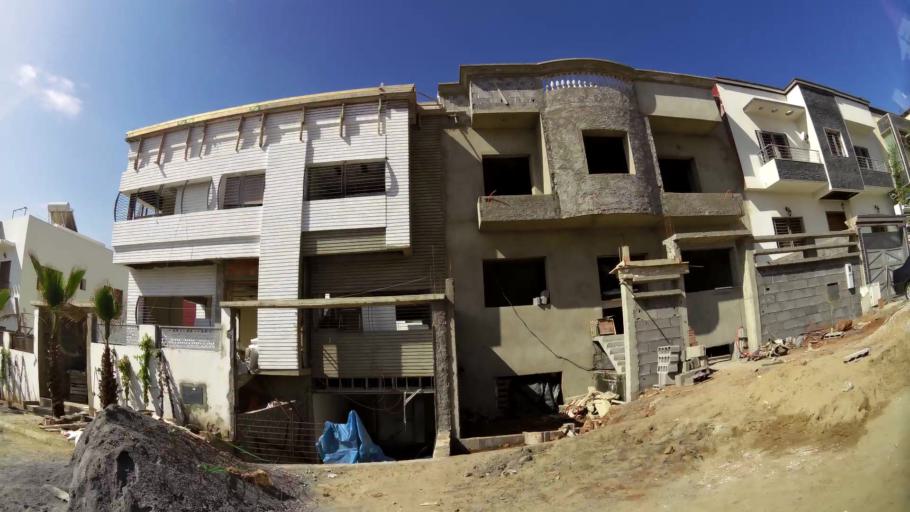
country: MA
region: Rabat-Sale-Zemmour-Zaer
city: Sale
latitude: 34.0655
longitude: -6.8051
